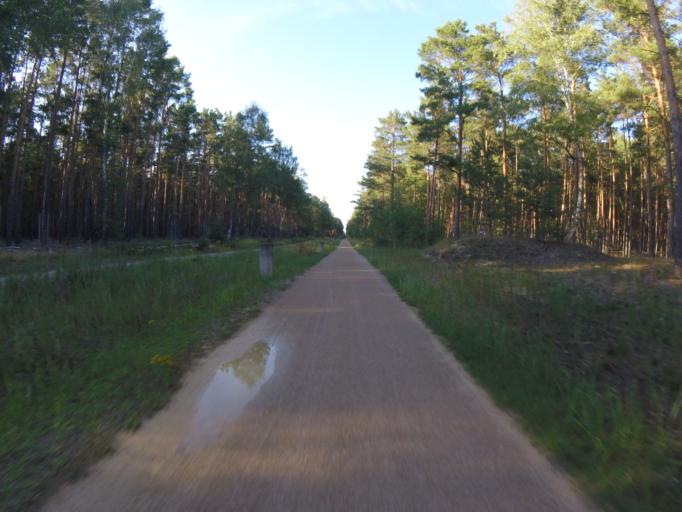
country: DE
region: Brandenburg
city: Halbe
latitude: 52.1879
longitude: 13.7599
